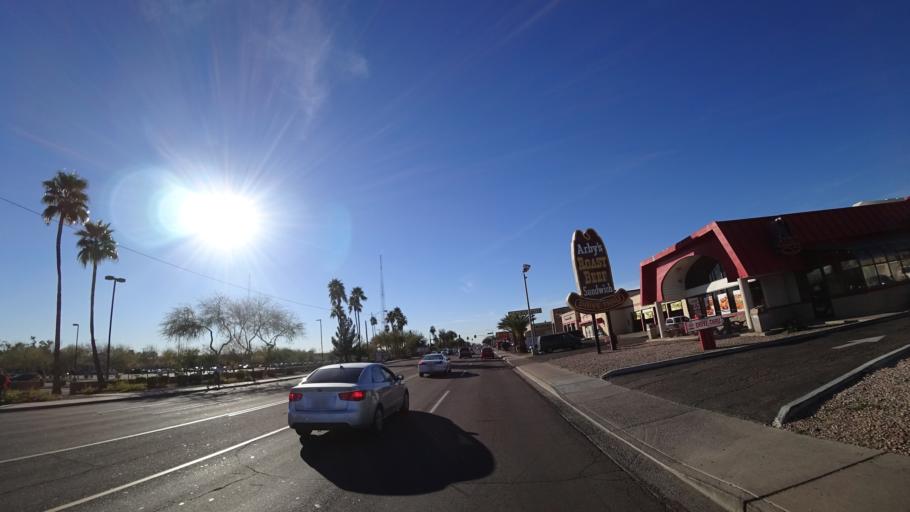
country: US
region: Arizona
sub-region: Maricopa County
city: Paradise Valley
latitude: 33.4805
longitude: -111.9982
